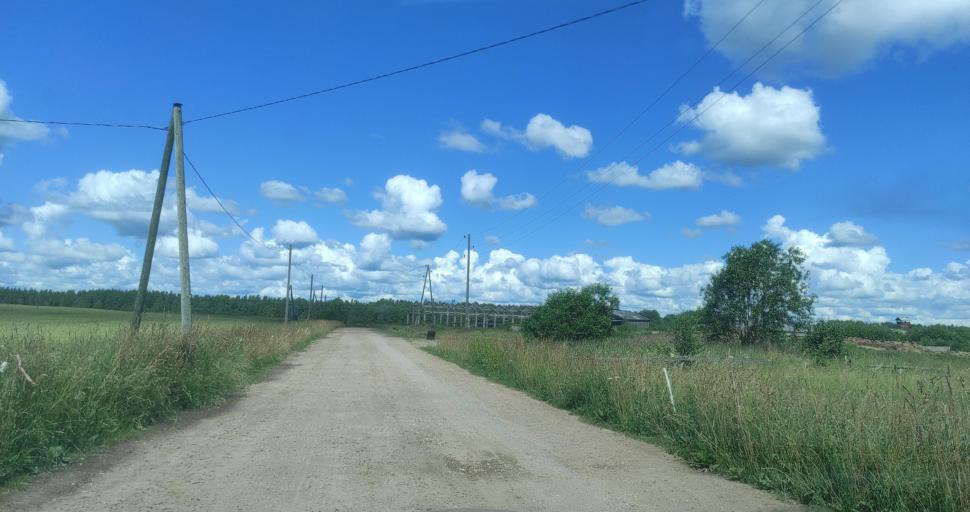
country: LV
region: Kuldigas Rajons
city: Kuldiga
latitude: 57.0012
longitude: 22.1309
